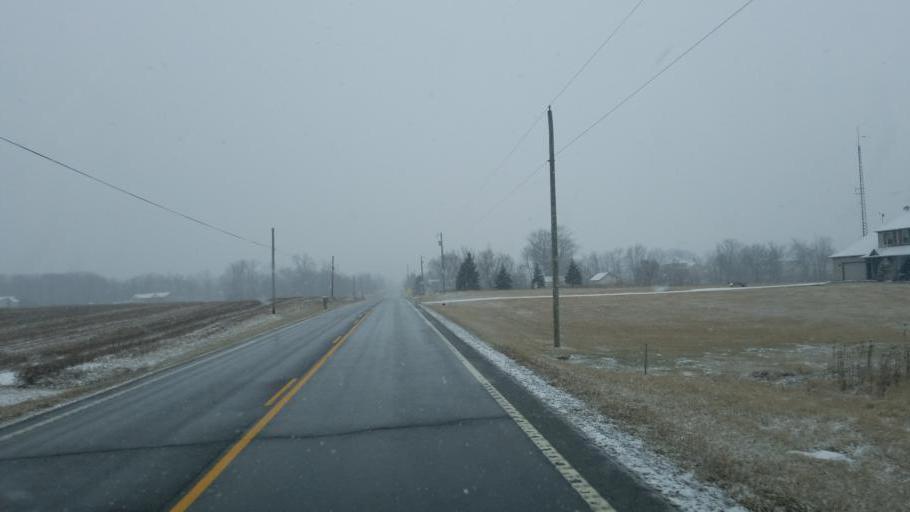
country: US
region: Ohio
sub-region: Defiance County
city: Hicksville
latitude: 41.3503
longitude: -84.7479
